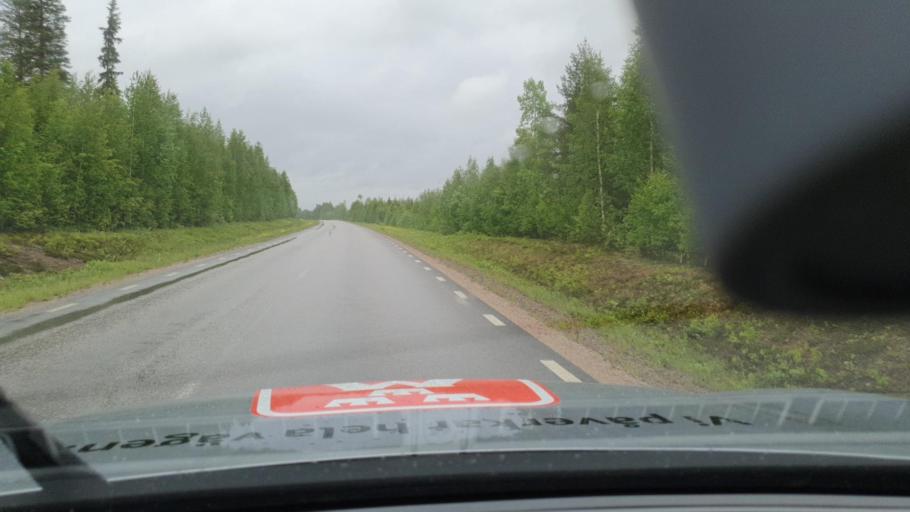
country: SE
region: Norrbotten
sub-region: Overtornea Kommun
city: OEvertornea
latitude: 66.3984
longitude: 23.5102
